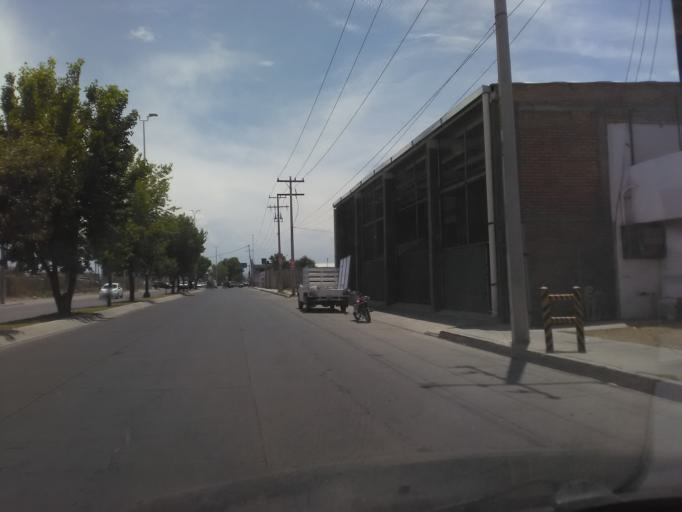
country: MX
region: Durango
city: Victoria de Durango
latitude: 24.0226
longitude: -104.6238
